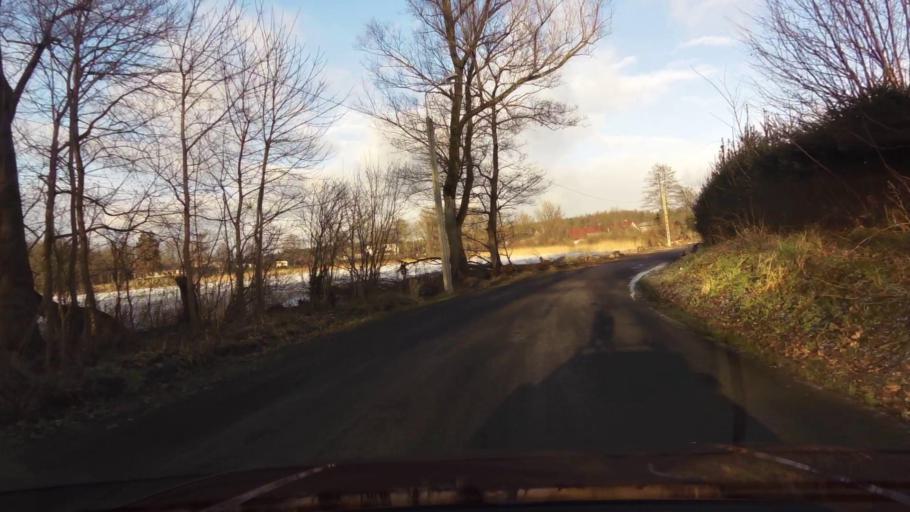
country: PL
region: West Pomeranian Voivodeship
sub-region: Koszalin
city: Koszalin
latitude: 54.0662
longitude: 16.1610
